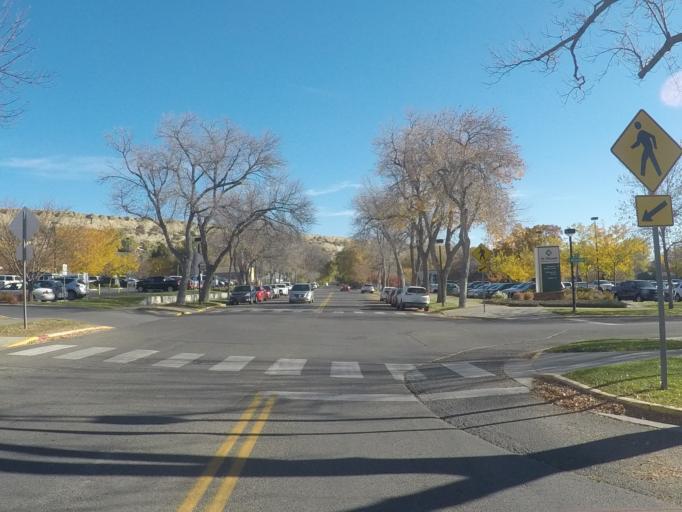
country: US
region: Montana
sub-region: Yellowstone County
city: Billings
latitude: 45.7934
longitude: -108.5174
